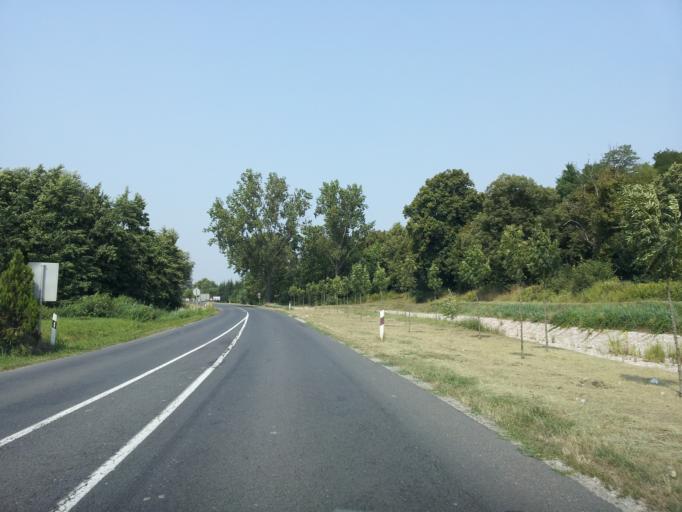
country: HU
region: Gyor-Moson-Sopron
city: Pannonhalma
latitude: 47.5110
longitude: 17.7605
